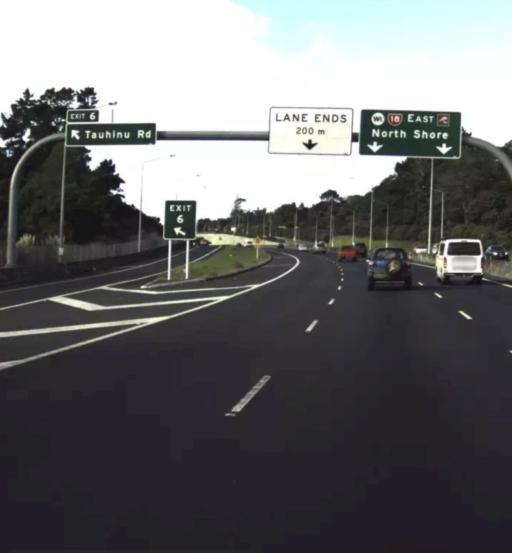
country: NZ
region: Auckland
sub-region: Auckland
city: North Shore
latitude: -36.7838
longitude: 174.6721
